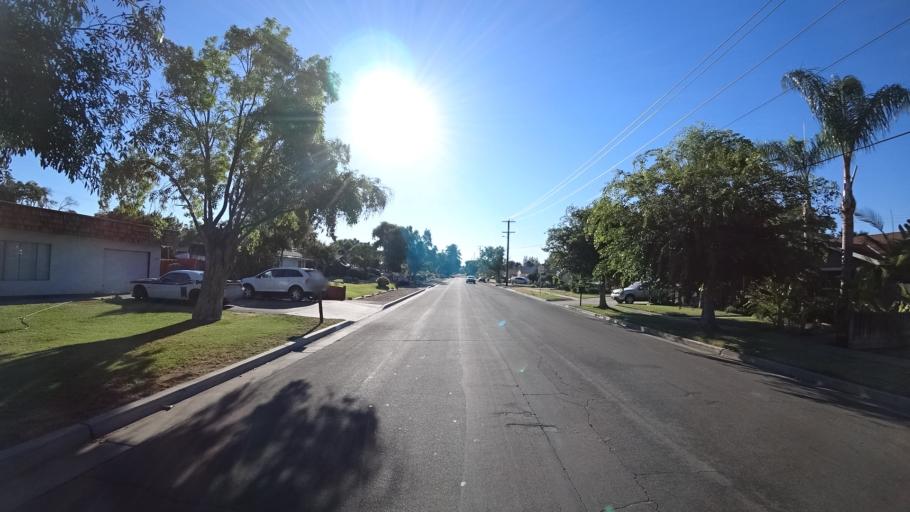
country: US
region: California
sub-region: Fresno County
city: Fresno
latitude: 36.8010
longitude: -119.8256
